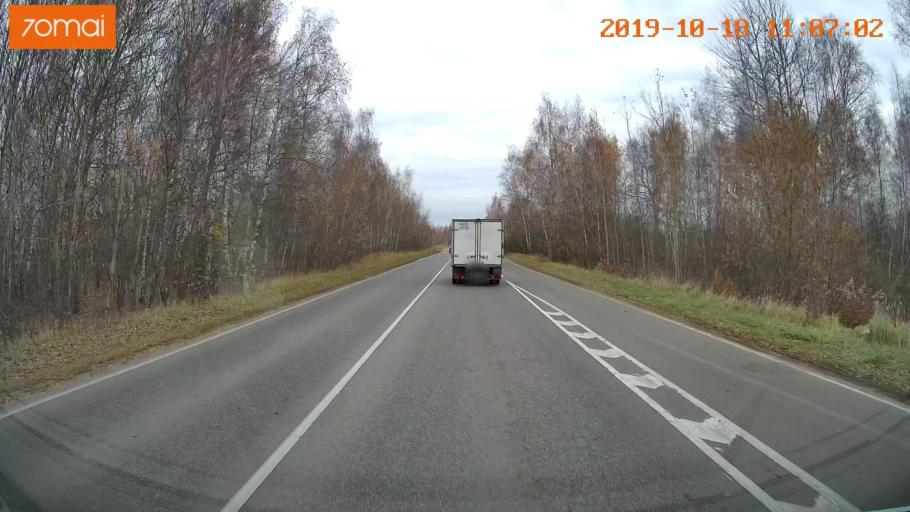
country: RU
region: Tula
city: Kimovsk
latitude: 53.9239
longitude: 38.5349
